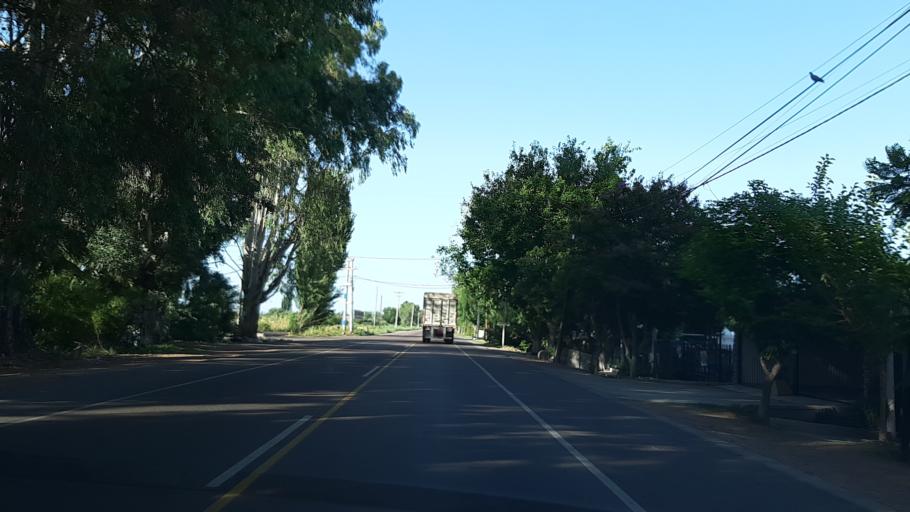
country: AR
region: Mendoza
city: San Martin
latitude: -33.0308
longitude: -68.5103
